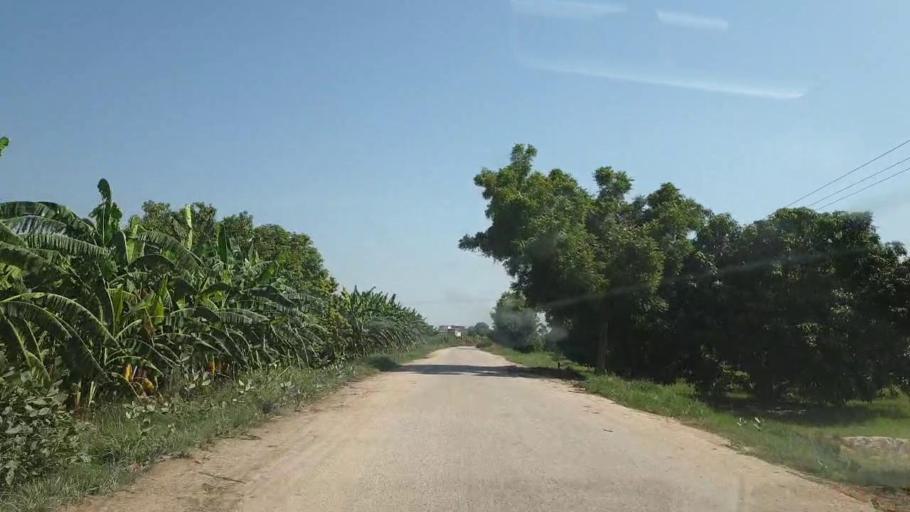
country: PK
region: Sindh
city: Tando Jam
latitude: 25.4030
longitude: 68.5849
